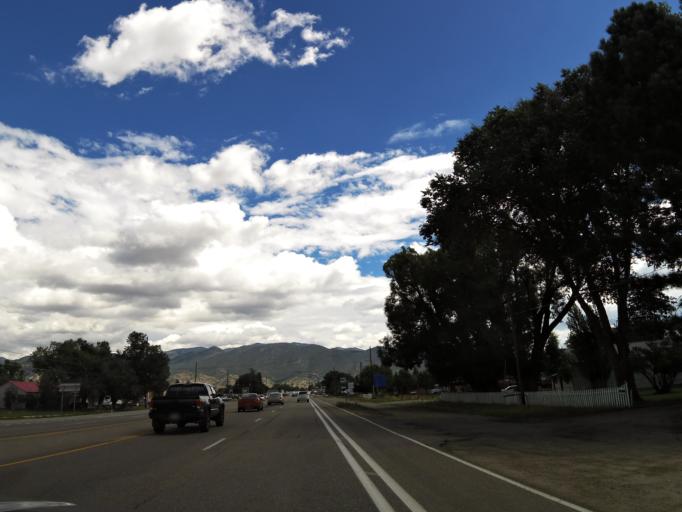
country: US
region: Colorado
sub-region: Chaffee County
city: Salida
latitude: 38.5234
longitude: -106.0195
